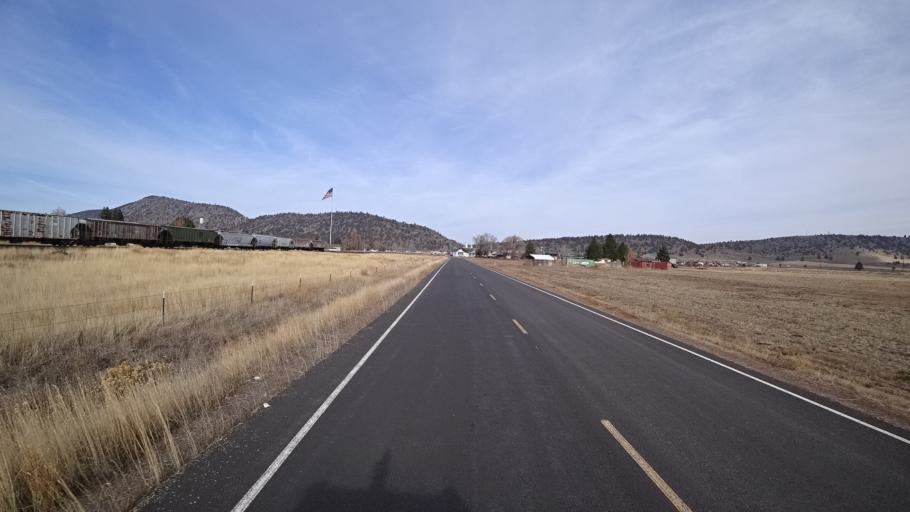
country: US
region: Oregon
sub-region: Klamath County
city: Klamath Falls
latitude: 41.9603
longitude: -121.9185
